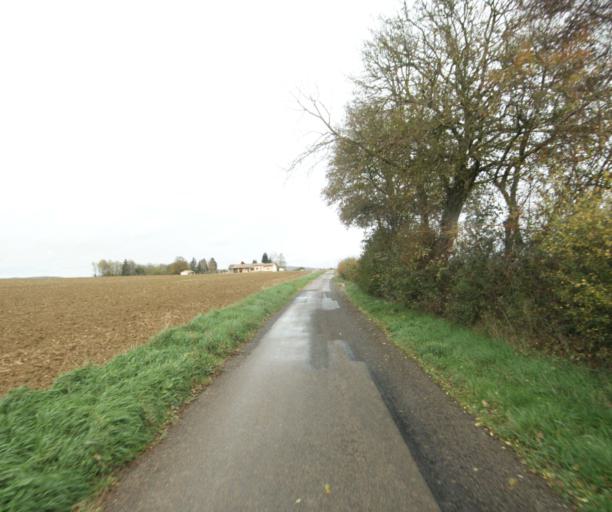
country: FR
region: Rhone-Alpes
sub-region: Departement de l'Ain
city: Pont-de-Vaux
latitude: 46.4695
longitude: 4.8731
